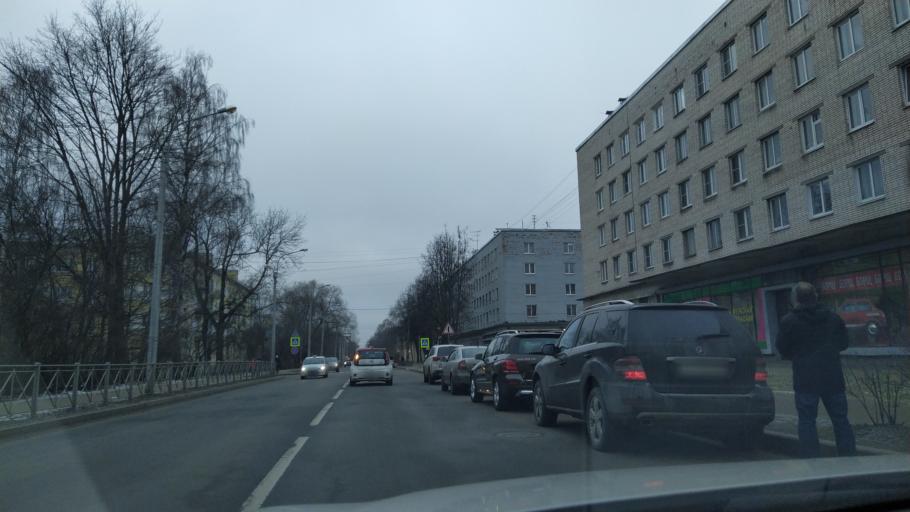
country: RU
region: St.-Petersburg
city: Pushkin
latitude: 59.7243
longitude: 30.4145
